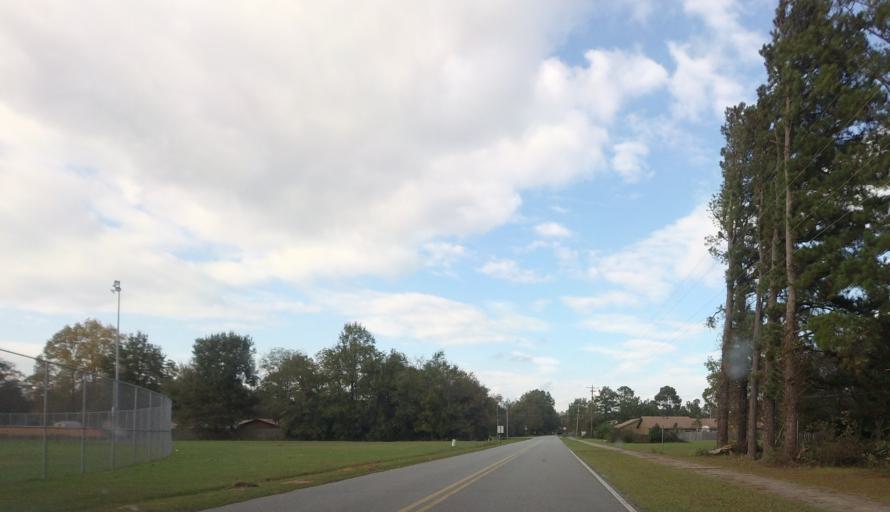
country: US
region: Georgia
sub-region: Houston County
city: Centerville
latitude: 32.6420
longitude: -83.6453
